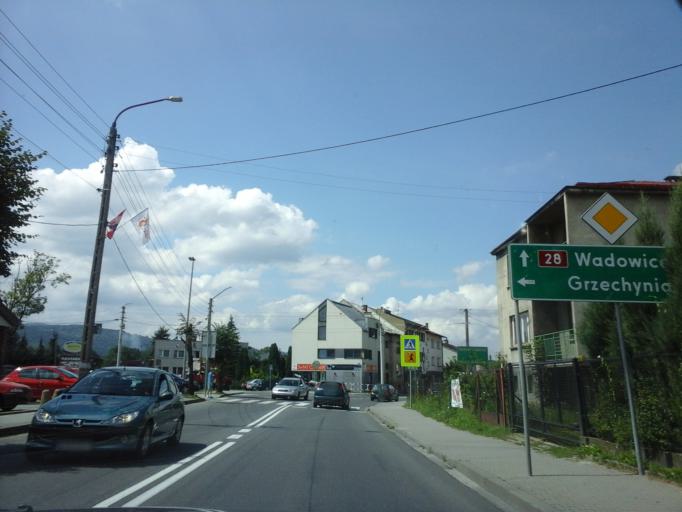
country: PL
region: Lesser Poland Voivodeship
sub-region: Powiat suski
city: Makow Podhalanski
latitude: 49.7298
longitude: 19.6728
